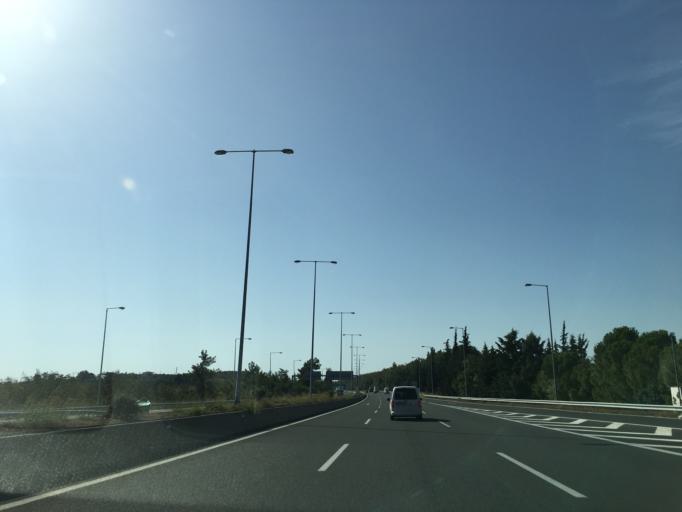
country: GR
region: Central Macedonia
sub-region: Nomos Pierias
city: Makrygialos
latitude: 40.4160
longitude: 22.5913
